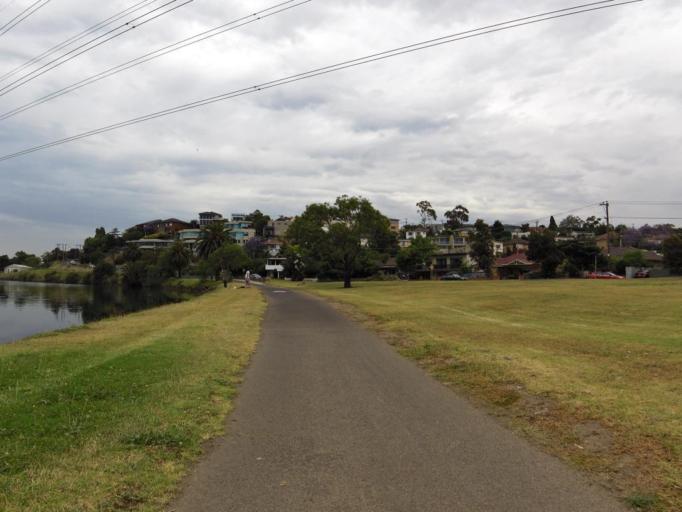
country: AU
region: Victoria
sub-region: Maribyrnong
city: Maribyrnong
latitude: -37.7717
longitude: 144.8963
